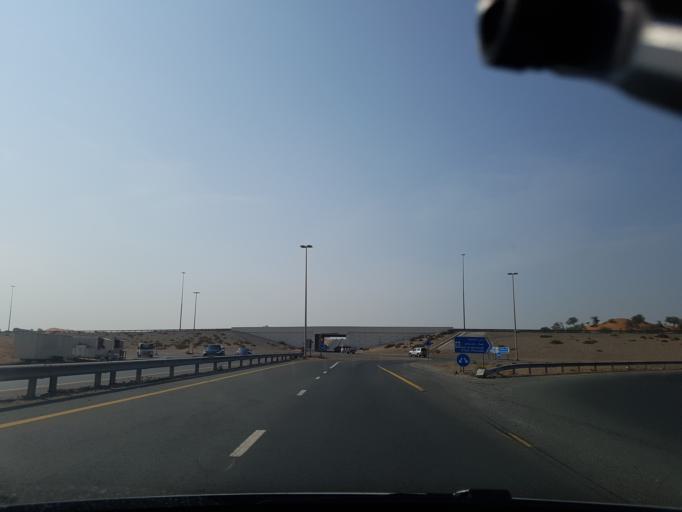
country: AE
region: Umm al Qaywayn
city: Umm al Qaywayn
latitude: 25.5277
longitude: 55.7257
